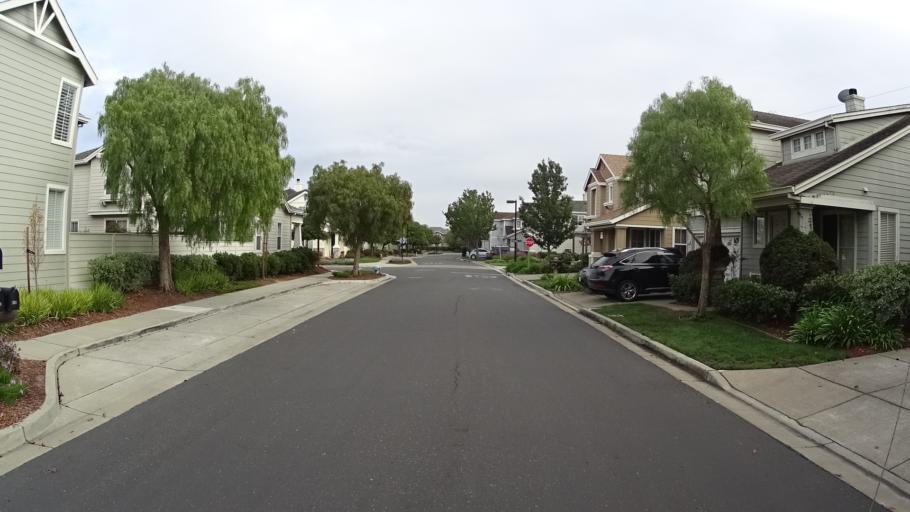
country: US
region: California
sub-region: San Mateo County
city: Redwood Shores
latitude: 37.5469
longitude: -122.2420
